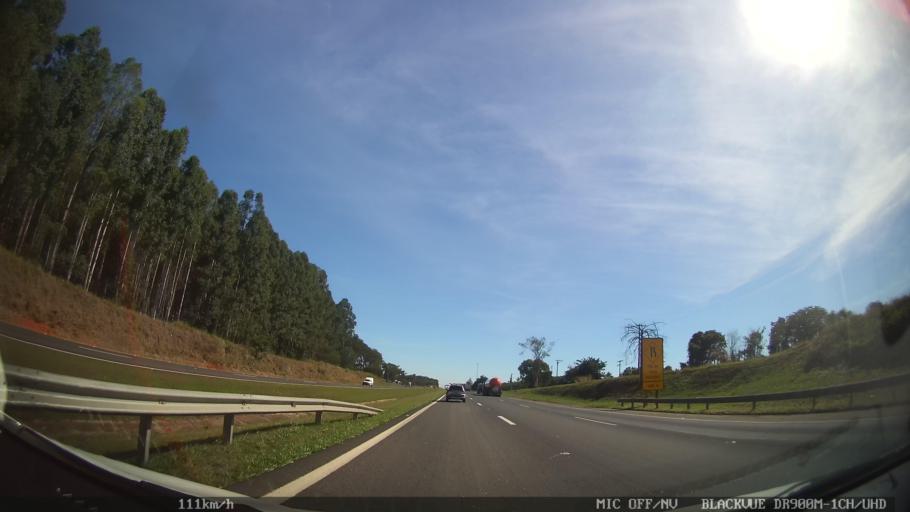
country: BR
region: Sao Paulo
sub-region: Santa Rita Do Passa Quatro
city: Santa Rita do Passa Quatro
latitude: -21.7813
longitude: -47.5314
